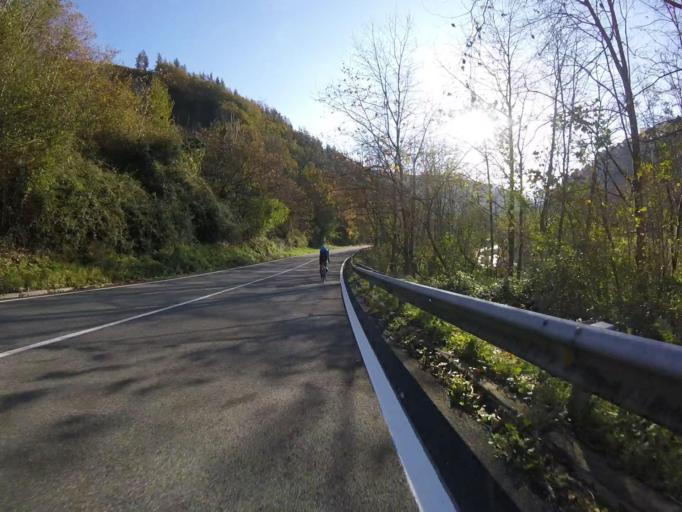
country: ES
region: Navarre
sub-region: Provincia de Navarra
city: Lesaka
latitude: 43.2516
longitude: -1.6745
